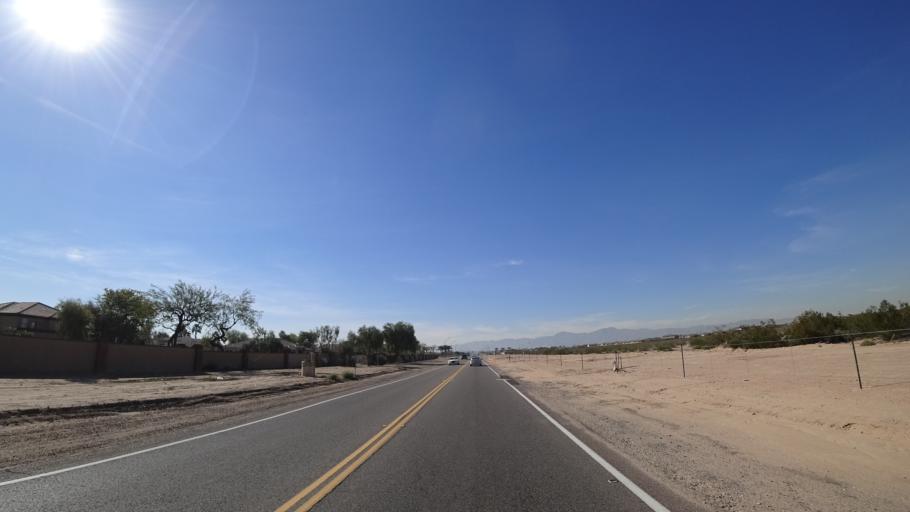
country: US
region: Arizona
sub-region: Maricopa County
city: Litchfield Park
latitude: 33.5083
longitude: -112.3661
